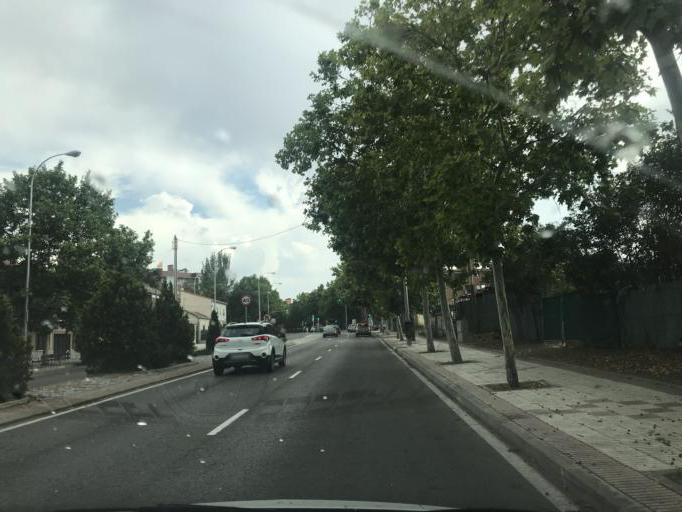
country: ES
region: Madrid
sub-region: Provincia de Madrid
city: Barajas de Madrid
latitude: 40.4767
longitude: -3.5821
